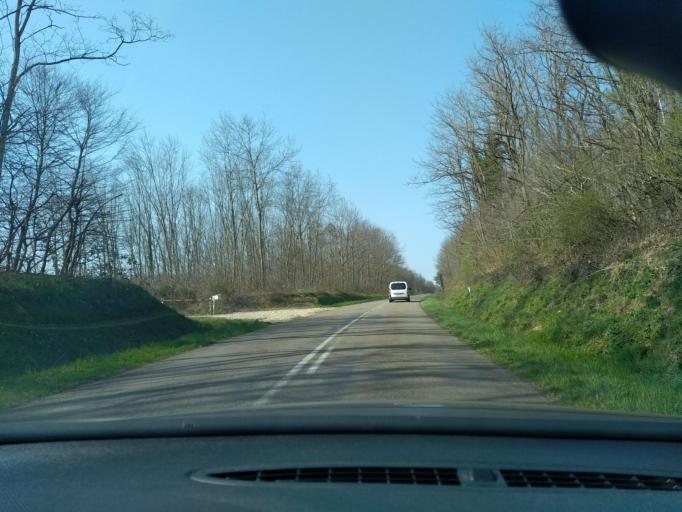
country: FR
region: Franche-Comte
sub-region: Departement du Jura
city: Dole
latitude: 47.0469
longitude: 5.5179
